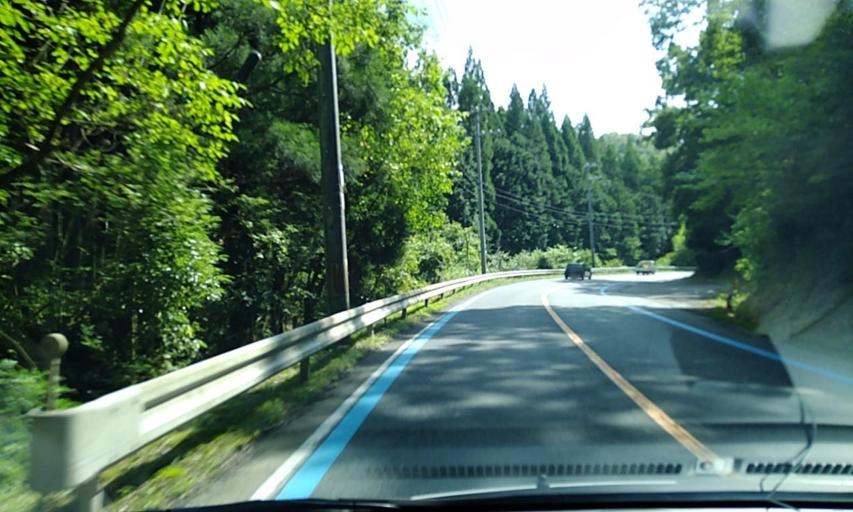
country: JP
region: Kyoto
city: Ayabe
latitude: 35.3050
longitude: 135.2972
